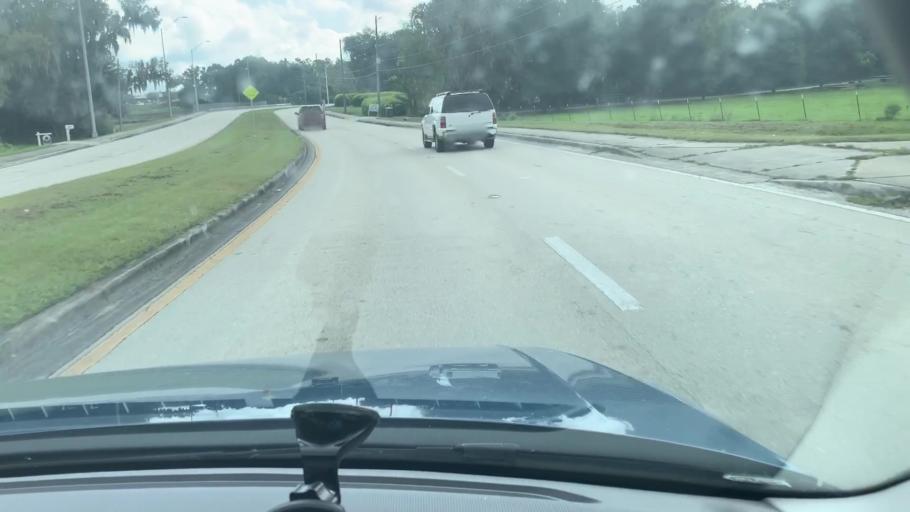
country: US
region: Florida
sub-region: Polk County
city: Kathleen
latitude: 28.0964
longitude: -82.0012
